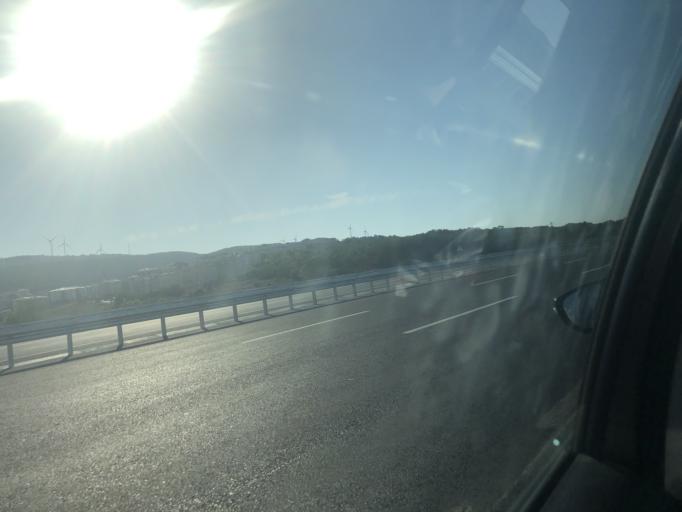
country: TR
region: Istanbul
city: Catalca
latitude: 41.1415
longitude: 28.4786
